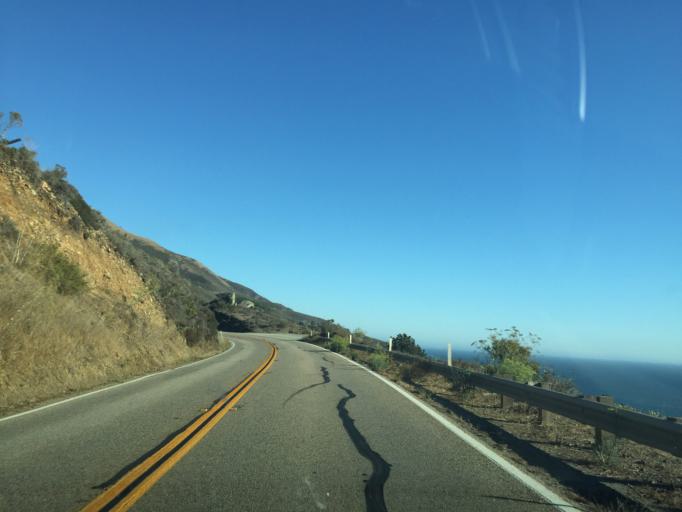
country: US
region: California
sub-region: Monterey County
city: King City
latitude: 35.8832
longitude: -121.4560
